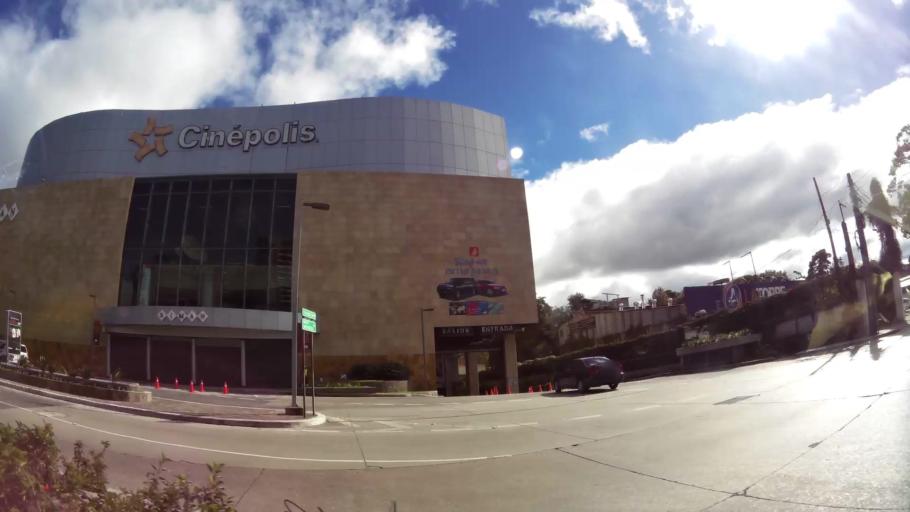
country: GT
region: Guatemala
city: Santa Catarina Pinula
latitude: 14.5979
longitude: -90.5077
